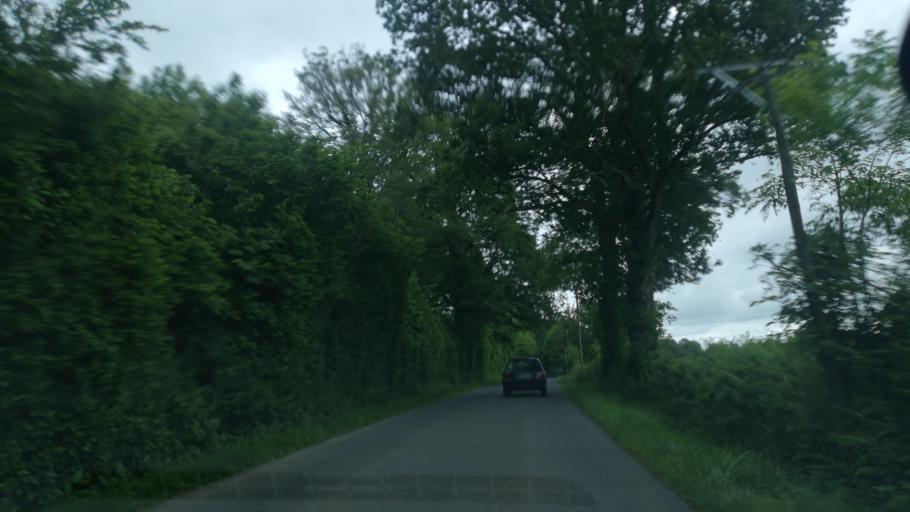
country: FR
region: Poitou-Charentes
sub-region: Departement des Deux-Sevres
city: Boisme
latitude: 46.7846
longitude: -0.4315
